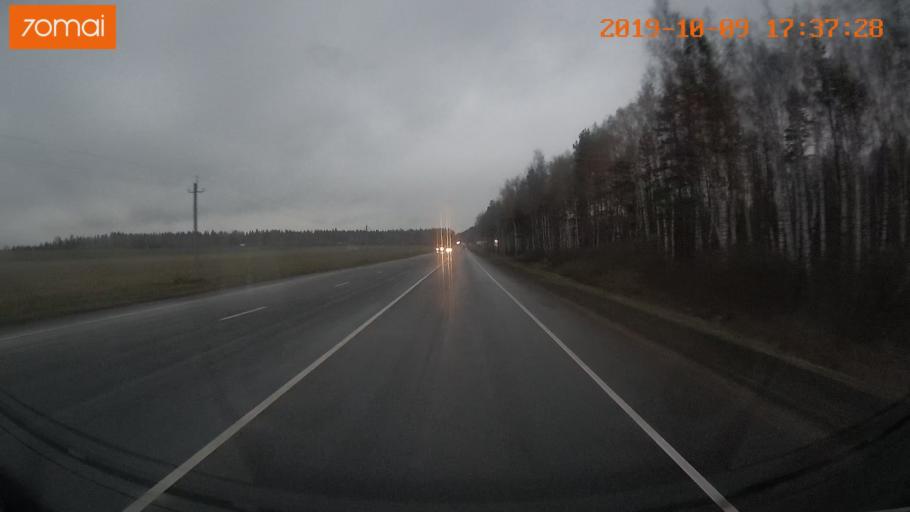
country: RU
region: Ivanovo
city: Bogorodskoye
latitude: 57.0712
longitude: 40.9779
